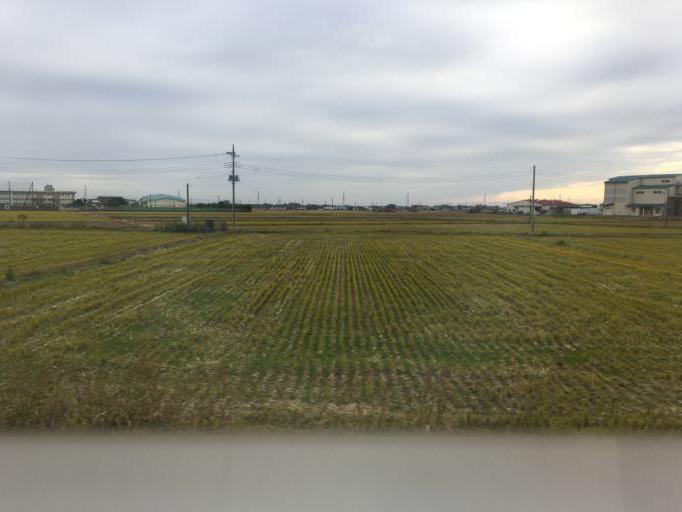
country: JP
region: Tochigi
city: Tochigi
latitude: 36.3571
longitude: 139.7690
